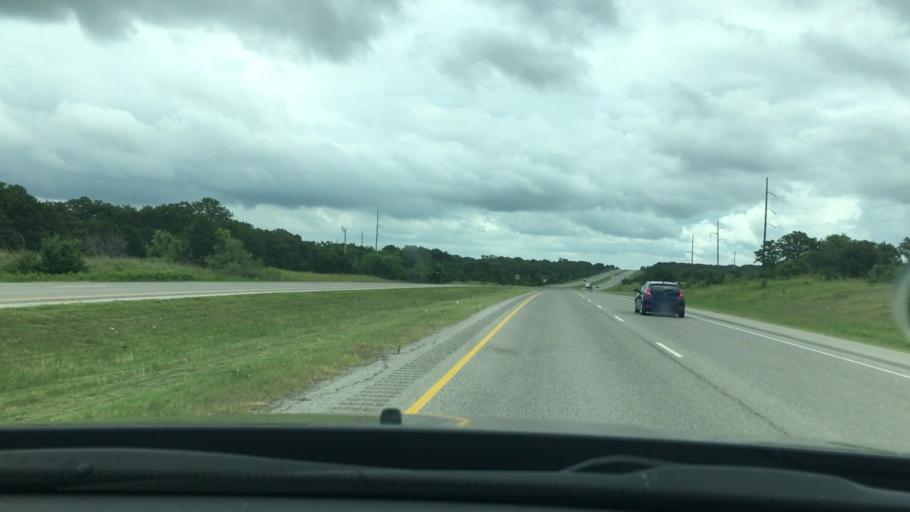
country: US
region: Oklahoma
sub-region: Carter County
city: Ardmore
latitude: 34.1329
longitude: -97.0929
